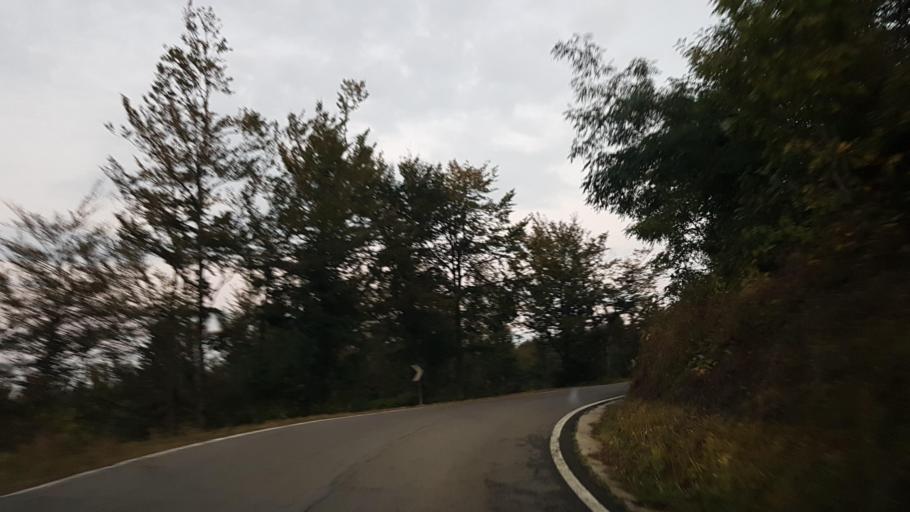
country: IT
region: Liguria
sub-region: Provincia di La Spezia
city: Varese Ligure
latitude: 44.4241
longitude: 9.6230
